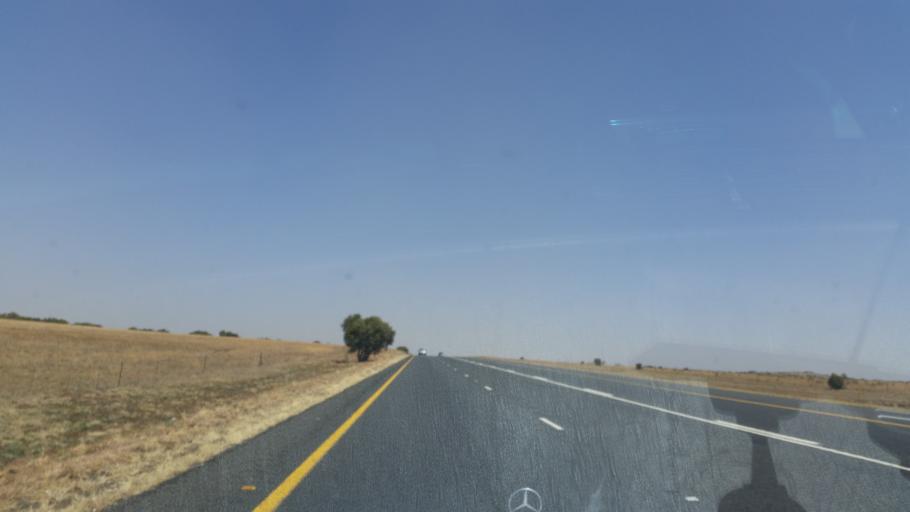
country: ZA
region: Orange Free State
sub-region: Lejweleputswa District Municipality
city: Winburg
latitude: -28.6987
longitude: 26.8020
